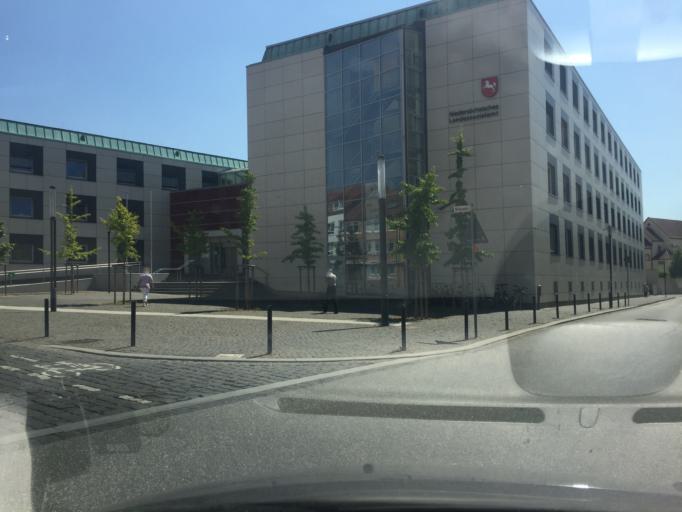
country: DE
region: Lower Saxony
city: Hildesheim
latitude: 52.1496
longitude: 9.9483
